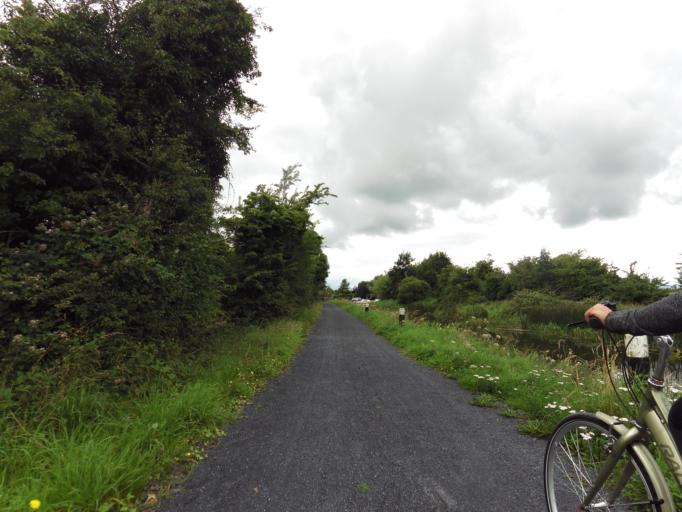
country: IE
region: Leinster
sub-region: An Iarmhi
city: An Muileann gCearr
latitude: 53.5338
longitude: -7.4657
